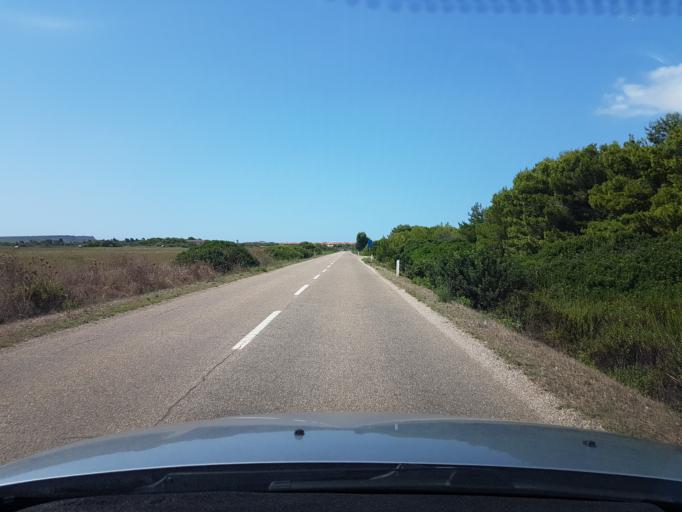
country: IT
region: Sardinia
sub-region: Provincia di Oristano
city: Riola Sardo
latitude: 40.0354
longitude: 8.4217
